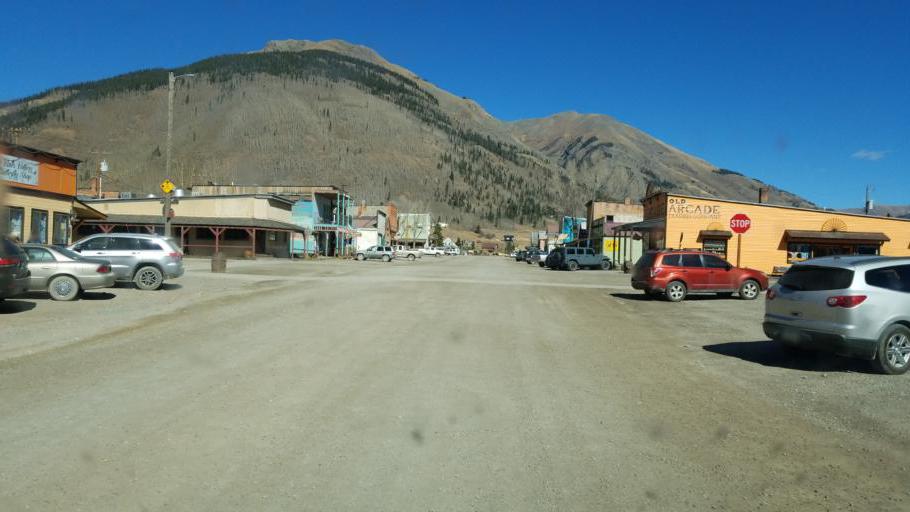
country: US
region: Colorado
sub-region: San Juan County
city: Silverton
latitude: 37.8108
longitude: -107.6637
